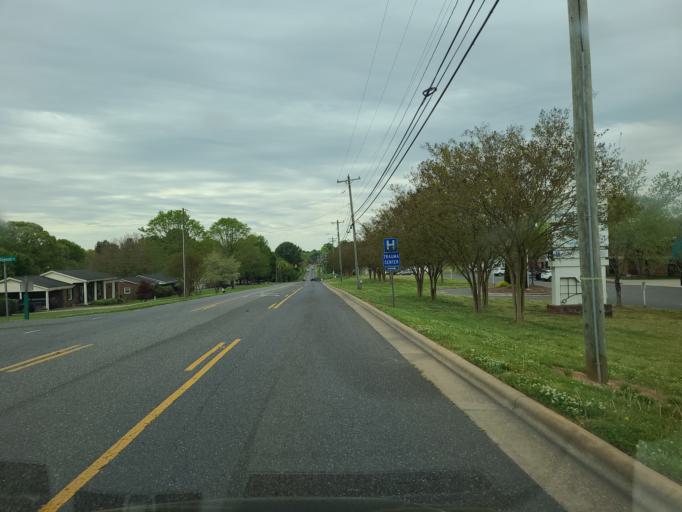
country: US
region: North Carolina
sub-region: Cleveland County
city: Shelby
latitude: 35.3023
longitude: -81.5062
